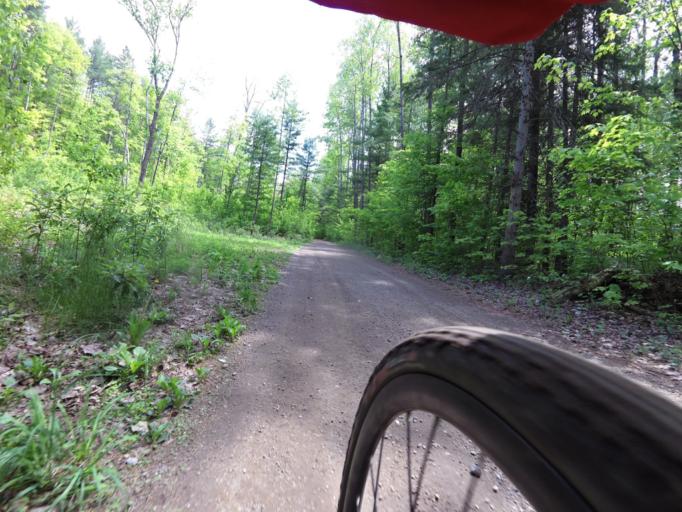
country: CA
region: Ontario
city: Renfrew
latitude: 45.2107
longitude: -76.6923
